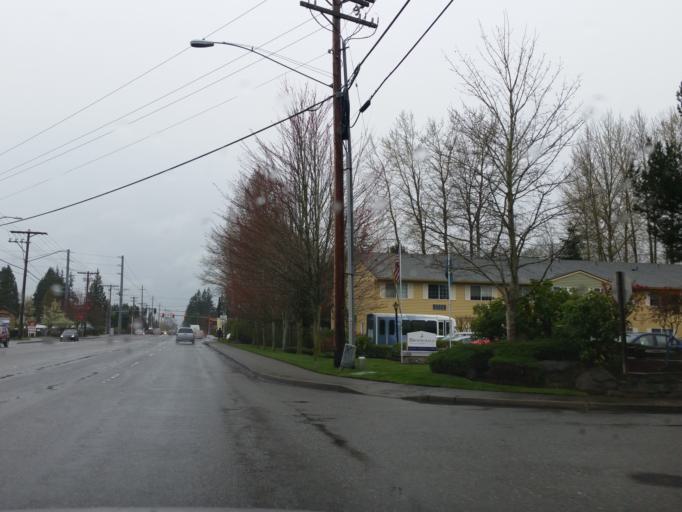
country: US
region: Washington
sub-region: Snohomish County
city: Martha Lake
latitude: 47.8946
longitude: -122.2388
